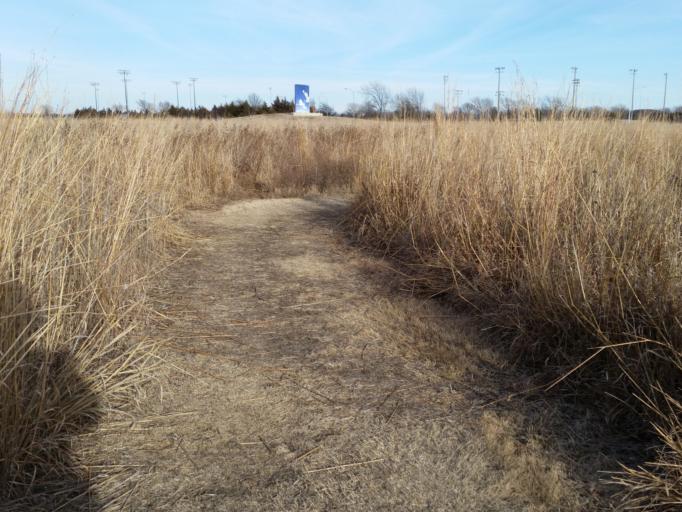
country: US
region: Kansas
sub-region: Harvey County
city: North Newton
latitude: 38.0615
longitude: -97.3389
